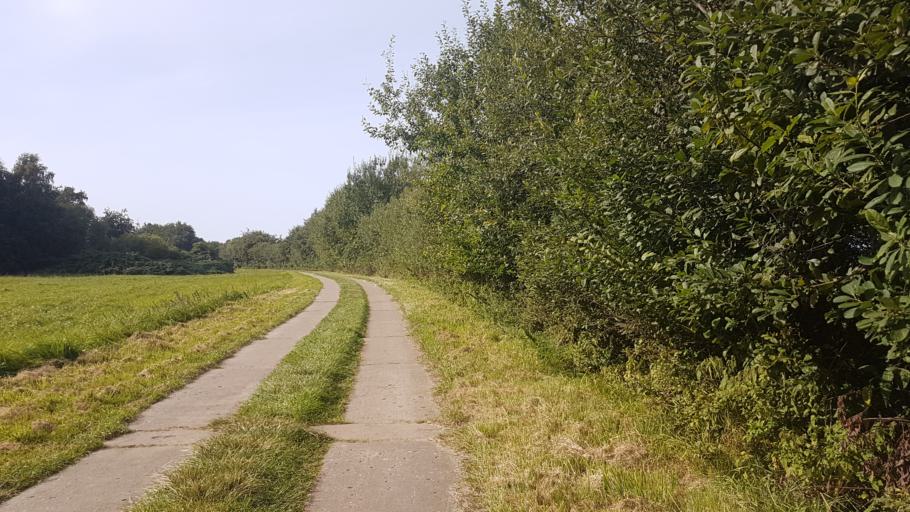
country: DE
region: Mecklenburg-Vorpommern
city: Gingst
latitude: 54.4357
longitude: 13.2032
